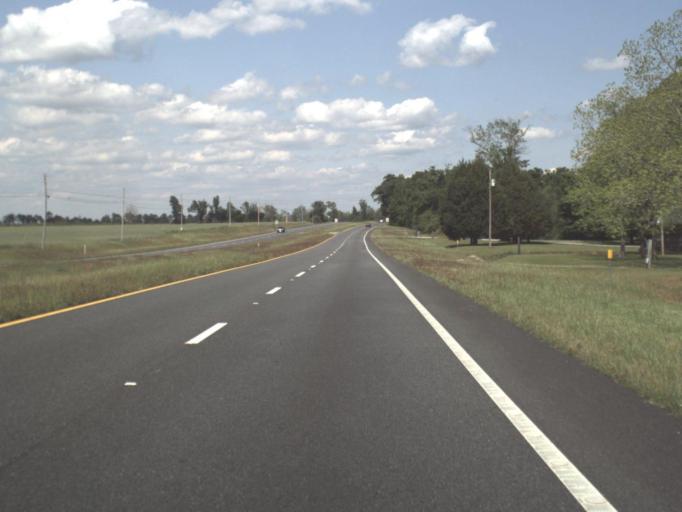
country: US
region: Florida
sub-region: Escambia County
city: Century
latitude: 30.9272
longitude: -87.3056
